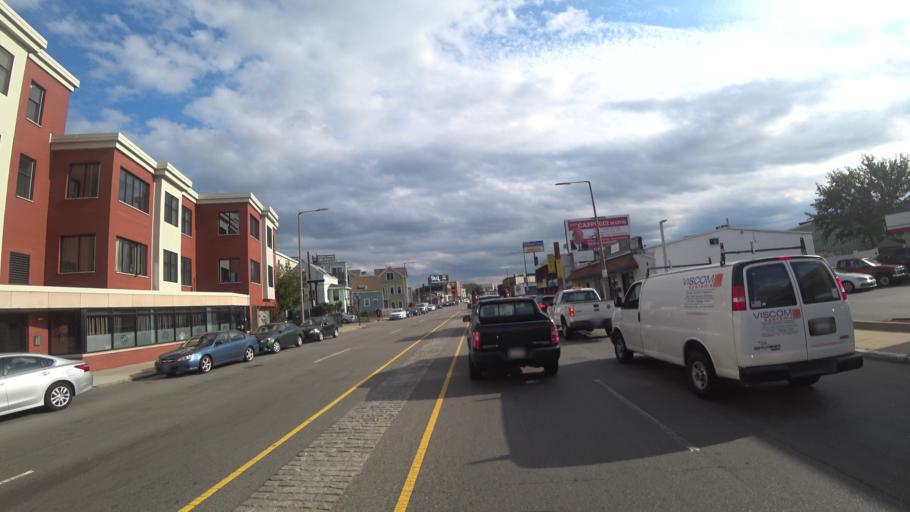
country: US
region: Massachusetts
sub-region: Suffolk County
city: South Boston
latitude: 42.3347
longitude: -71.0550
